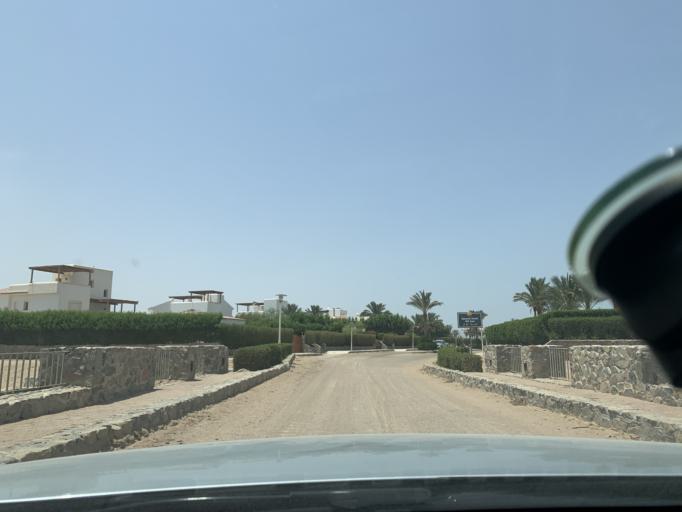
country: EG
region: Red Sea
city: El Gouna
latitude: 27.3699
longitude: 33.6708
